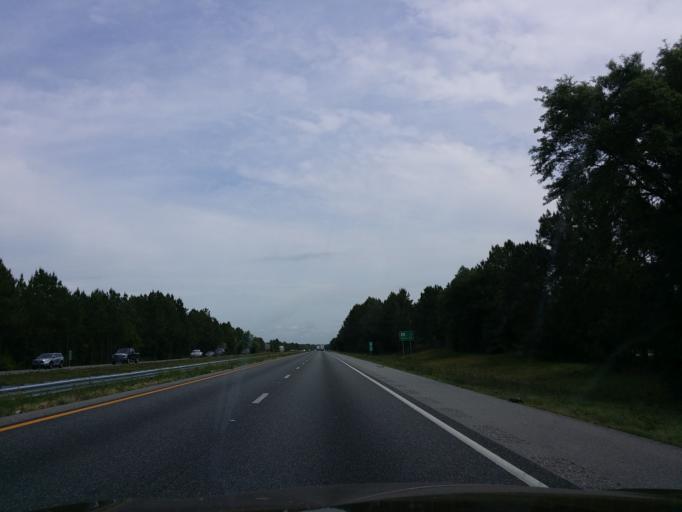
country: US
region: Florida
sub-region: Hernando County
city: Hill 'n Dale
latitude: 28.5365
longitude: -82.2369
